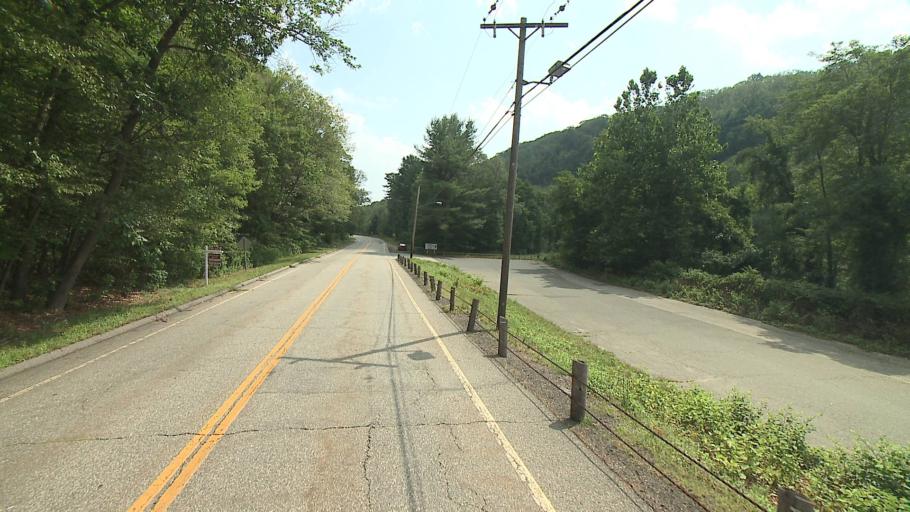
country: US
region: Connecticut
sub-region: Litchfield County
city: Oakville
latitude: 41.6250
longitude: -73.0673
